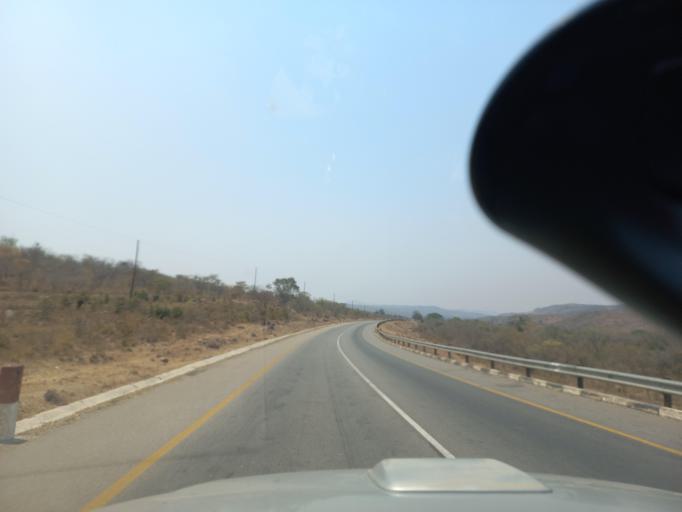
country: ZM
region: Lusaka
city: Kafue
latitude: -15.8865
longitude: 28.3232
